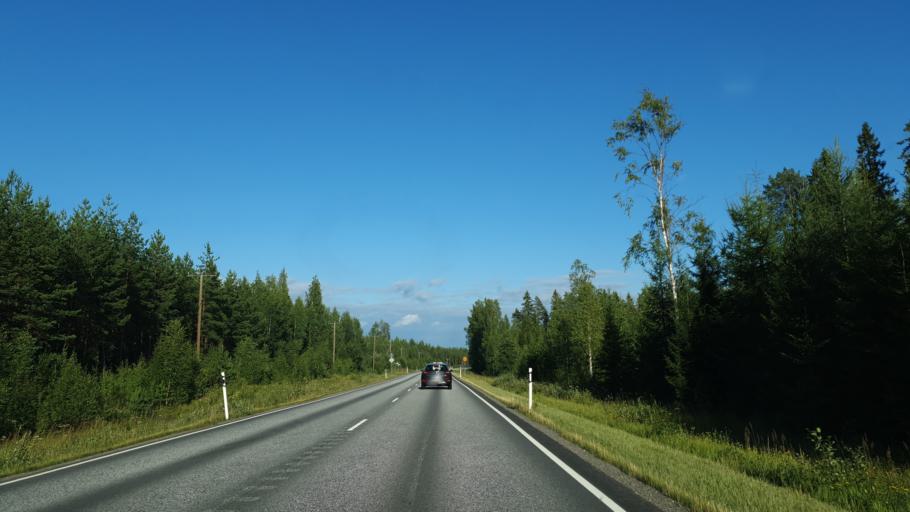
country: FI
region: North Karelia
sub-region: Joensuu
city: Outokumpu
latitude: 62.5327
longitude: 28.9658
